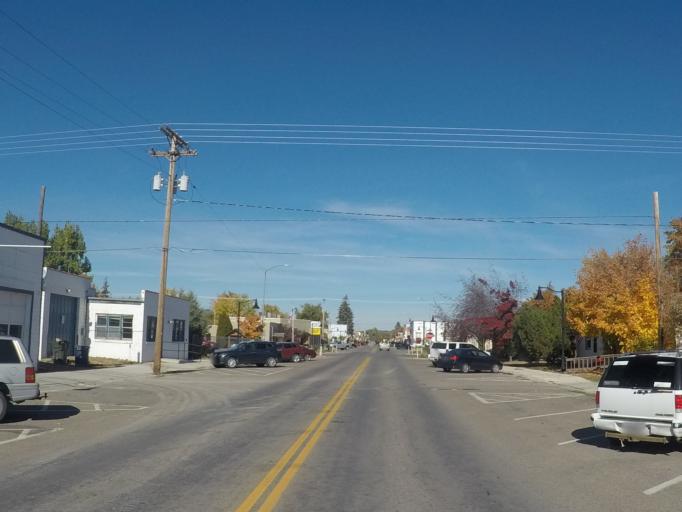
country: US
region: Montana
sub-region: Lake County
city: Polson
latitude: 47.6895
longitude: -114.1634
